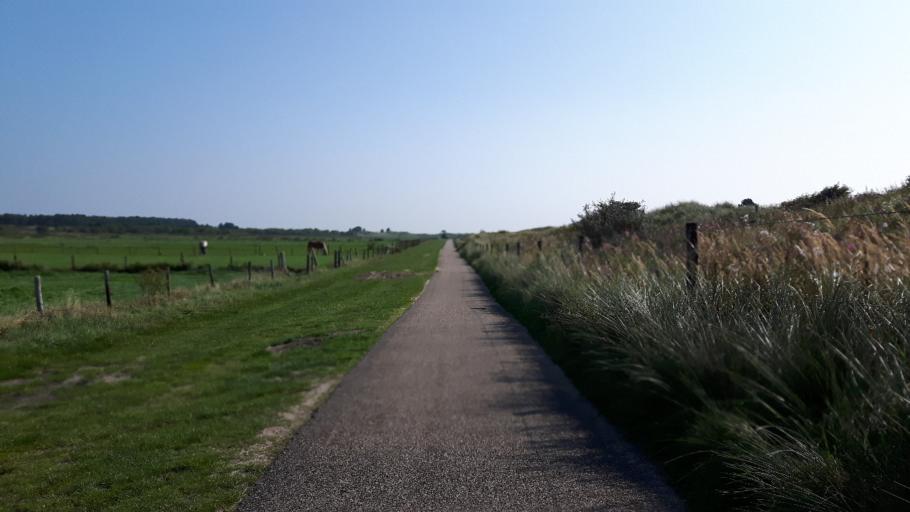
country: NL
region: Friesland
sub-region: Gemeente Ameland
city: Nes
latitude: 53.4554
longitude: 5.8094
